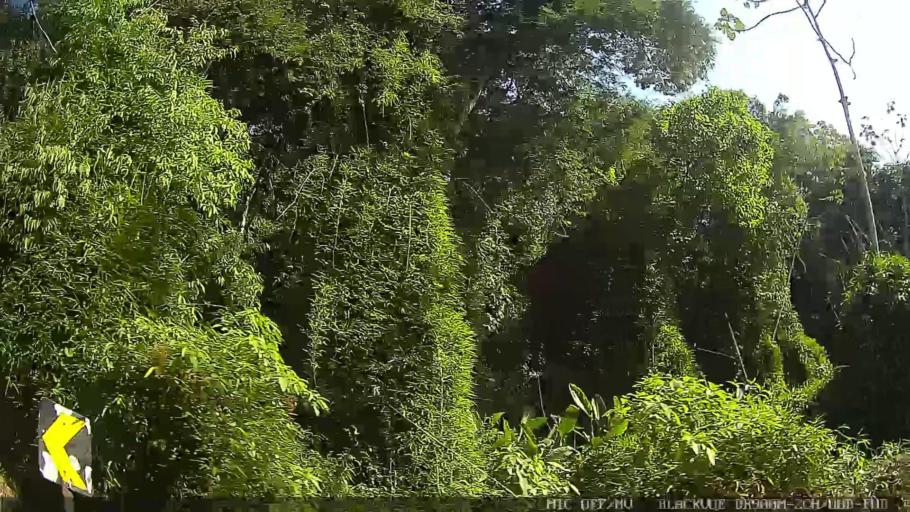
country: BR
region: Sao Paulo
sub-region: Santos
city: Santos
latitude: -24.0028
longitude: -46.3119
